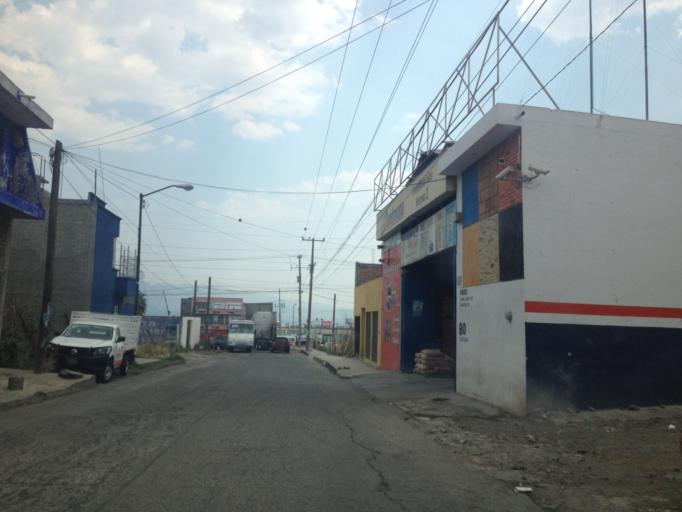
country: MX
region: Michoacan
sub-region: Morelia
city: San Antonio
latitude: 19.7065
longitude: -101.2425
